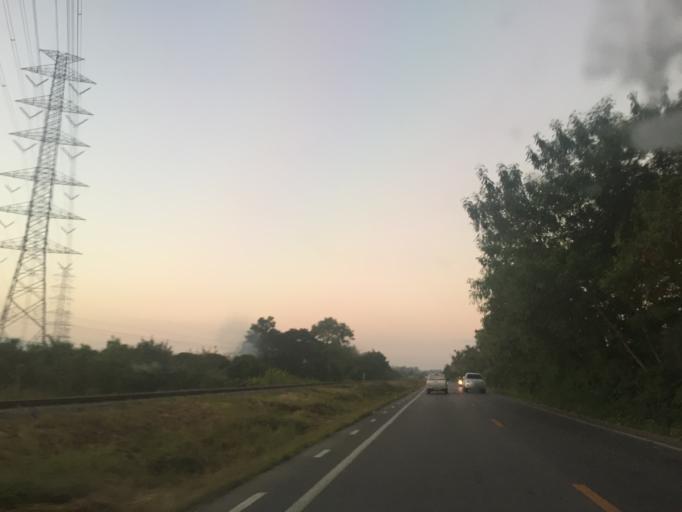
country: TH
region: Chiang Mai
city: Saraphi
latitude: 18.6587
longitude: 99.0446
